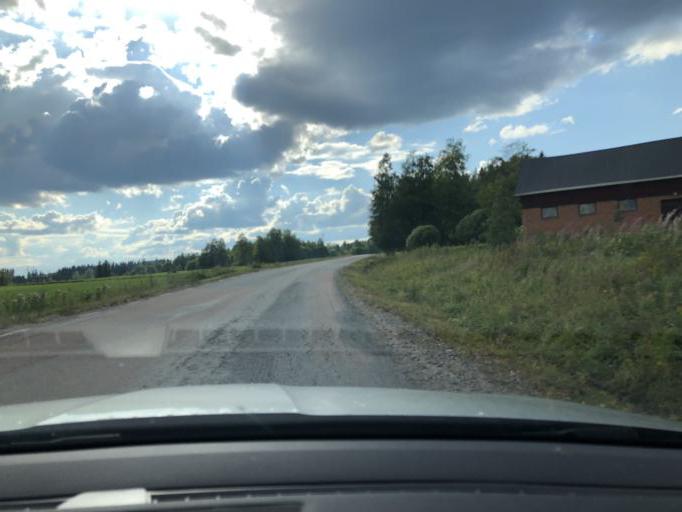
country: SE
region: Vaesternorrland
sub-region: Solleftea Kommun
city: Solleftea
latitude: 63.2017
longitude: 17.1185
